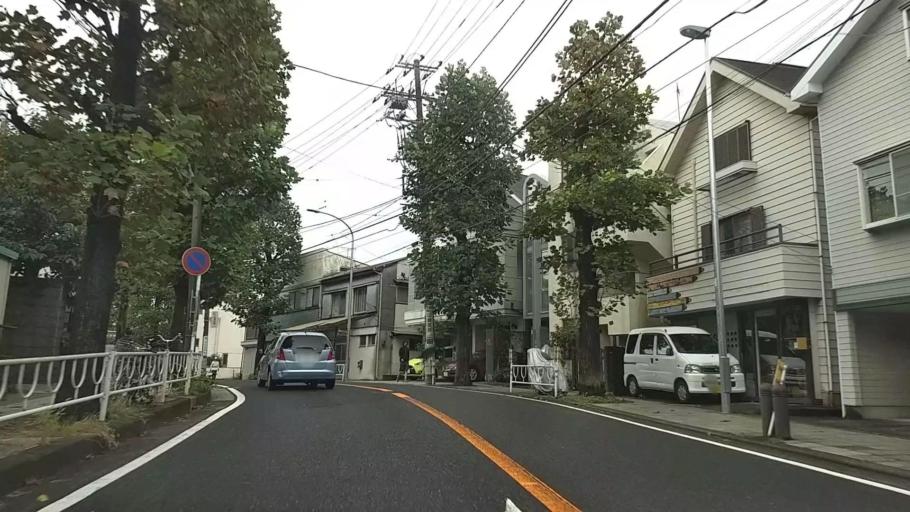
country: JP
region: Kanagawa
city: Yokohama
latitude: 35.4282
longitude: 139.6386
